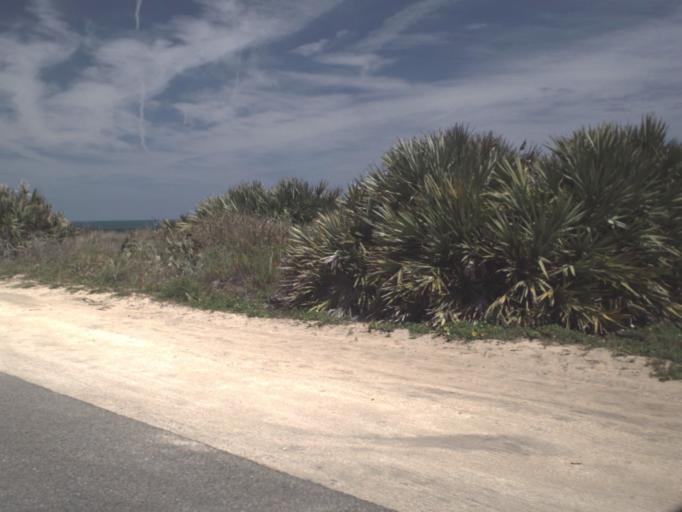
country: US
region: Florida
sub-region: Flagler County
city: Flagler Beach
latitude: 29.4923
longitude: -81.1330
